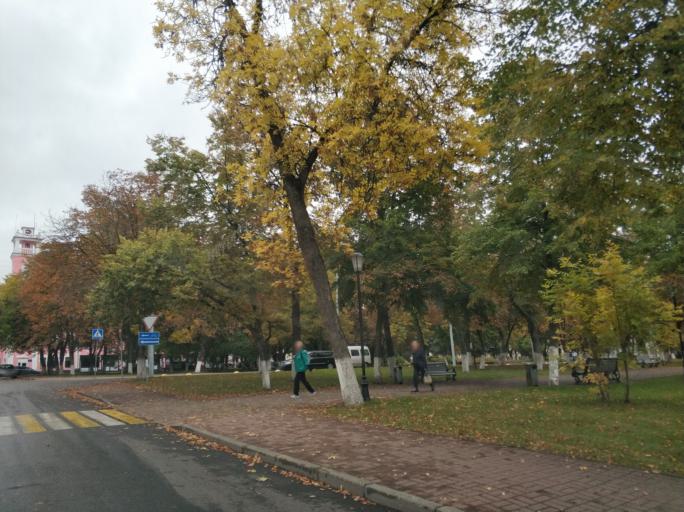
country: BY
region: Vitebsk
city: Polatsk
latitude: 55.4849
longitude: 28.7723
